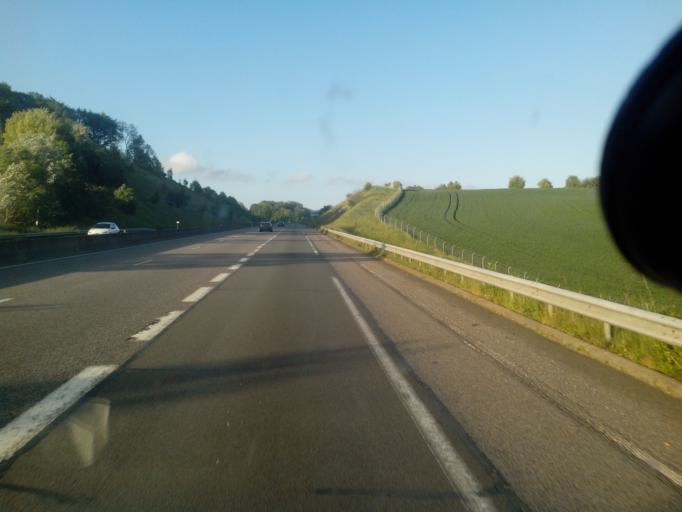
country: FR
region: Haute-Normandie
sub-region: Departement de la Seine-Maritime
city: Neufchatel-en-Bray
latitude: 49.7304
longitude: 1.4606
